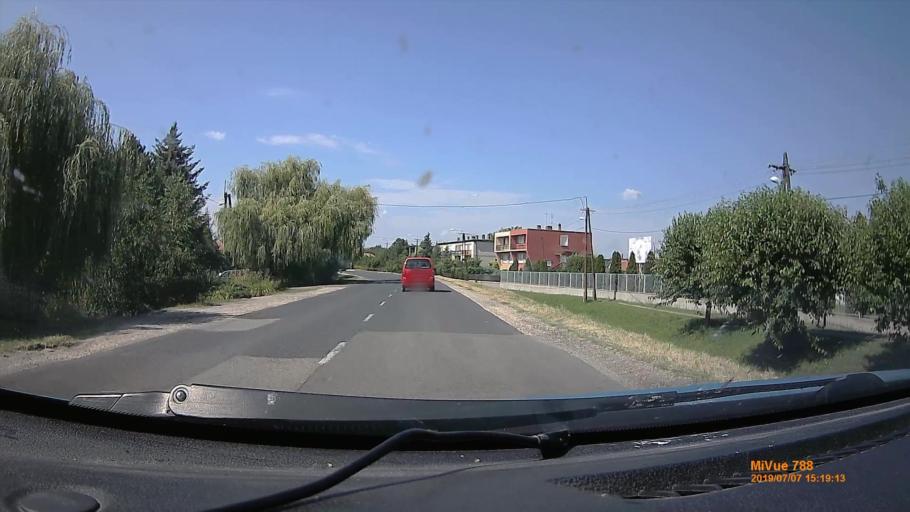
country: HU
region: Jasz-Nagykun-Szolnok
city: Jaszalsoszentgyorgy
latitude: 47.3616
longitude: 20.0938
